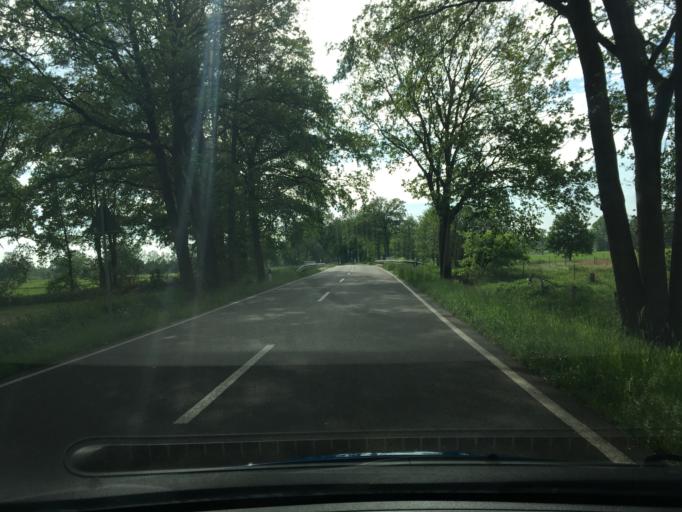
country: DE
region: Lower Saxony
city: Kalbe
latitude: 53.2793
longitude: 9.5913
